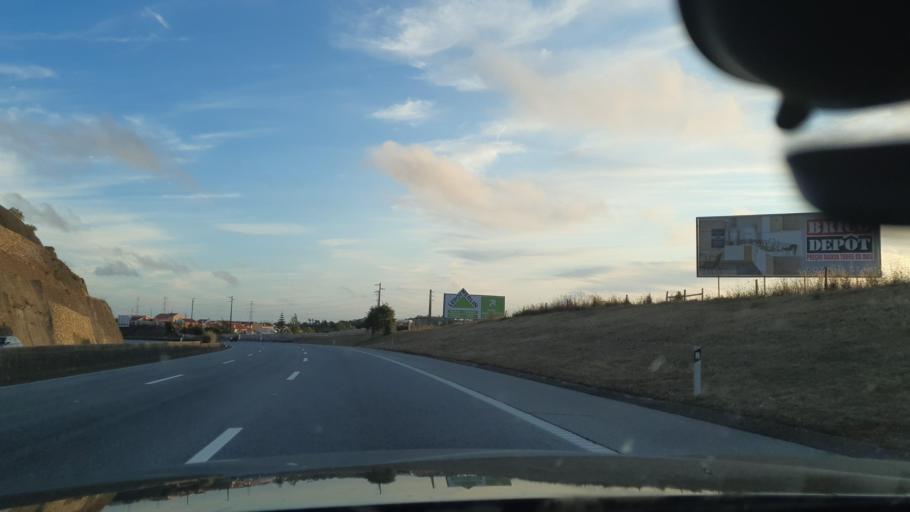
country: PT
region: Lisbon
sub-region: Odivelas
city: Canecas
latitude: 38.8082
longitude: -9.2346
